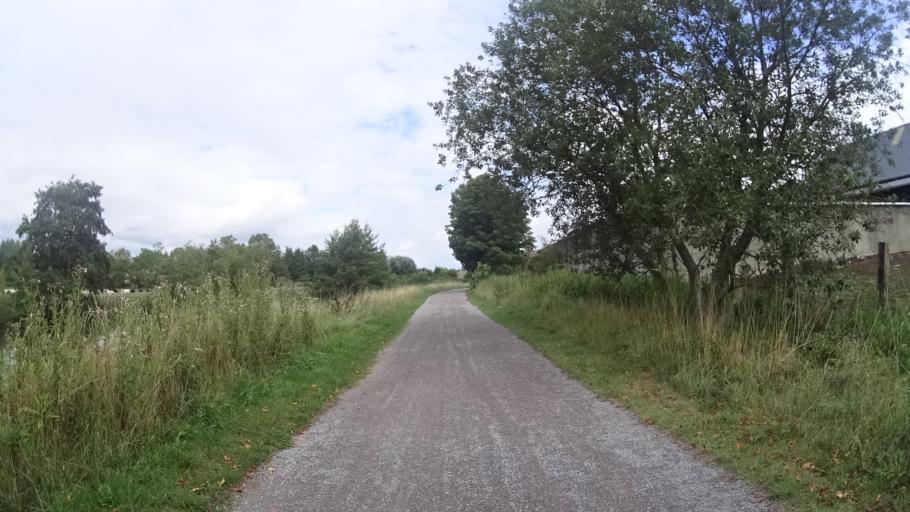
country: FR
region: Nord-Pas-de-Calais
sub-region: Departement du Nord
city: Aulnoye-Aymeries
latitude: 50.2114
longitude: 3.8288
